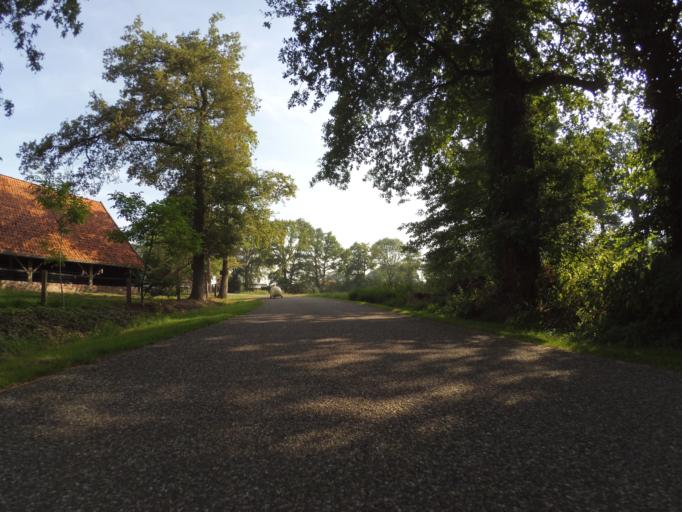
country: DE
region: Lower Saxony
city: Getelo
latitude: 52.3864
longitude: 6.8724
